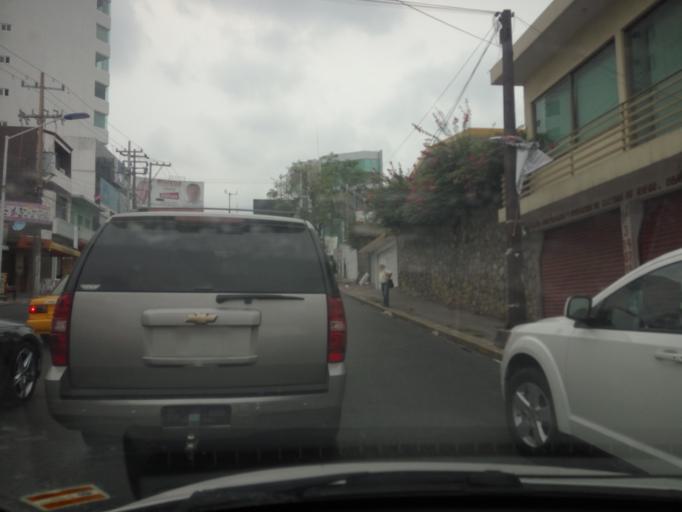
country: MX
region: Tabasco
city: Villahermosa
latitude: 17.9959
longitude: -92.9269
